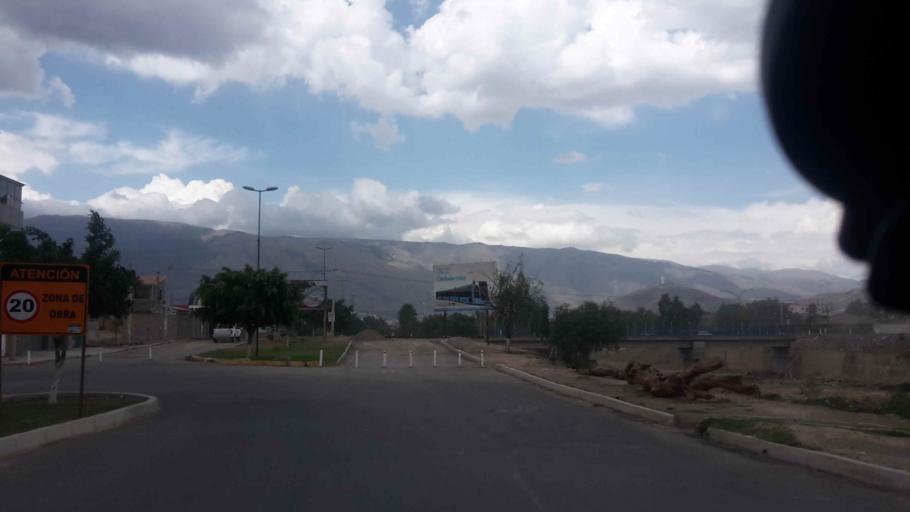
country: BO
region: Cochabamba
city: Cochabamba
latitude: -17.4068
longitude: -66.1726
